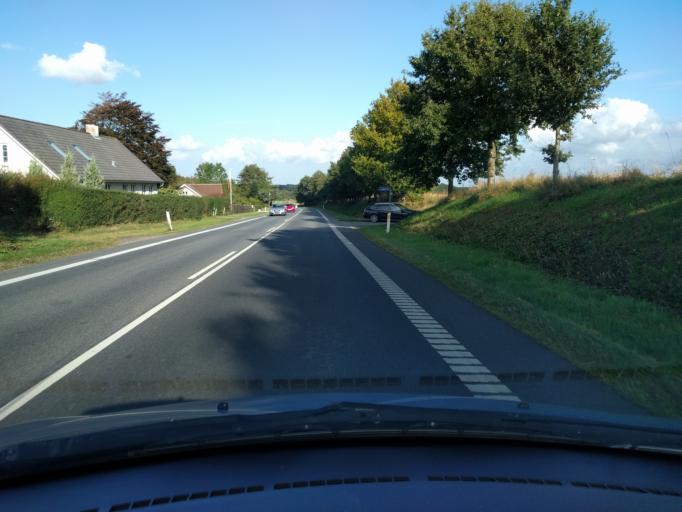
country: DK
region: South Denmark
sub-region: Assens Kommune
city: Glamsbjerg
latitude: 55.2780
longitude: 10.1520
